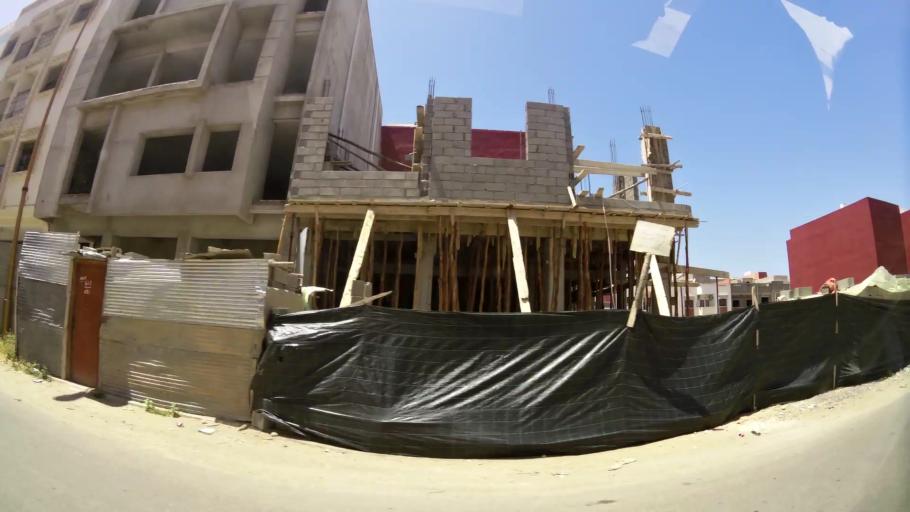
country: MA
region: Oued ed Dahab-Lagouira
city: Dakhla
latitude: 30.4305
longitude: -9.5527
